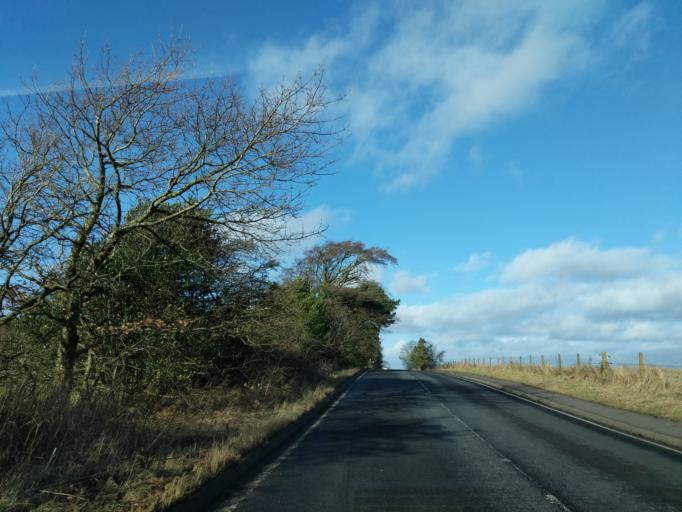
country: GB
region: Scotland
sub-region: West Lothian
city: Kirknewton
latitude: 55.8710
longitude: -3.4061
